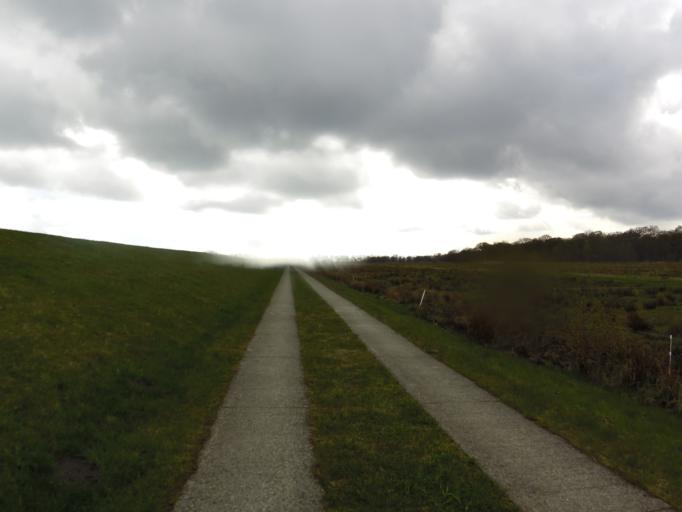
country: DE
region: Mecklenburg-Vorpommern
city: Barth
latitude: 54.4257
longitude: 12.8014
